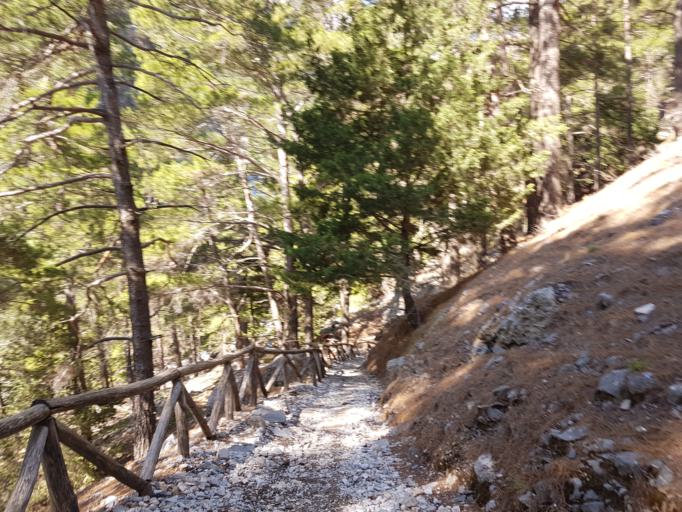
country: GR
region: Crete
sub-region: Nomos Chanias
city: Perivolia
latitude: 35.3070
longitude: 23.9274
